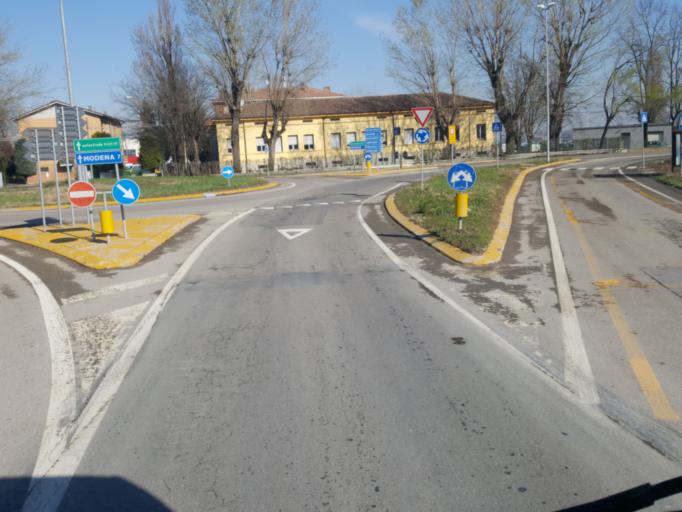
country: IT
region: Emilia-Romagna
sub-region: Provincia di Modena
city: Albareto
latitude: 44.6664
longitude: 10.9895
